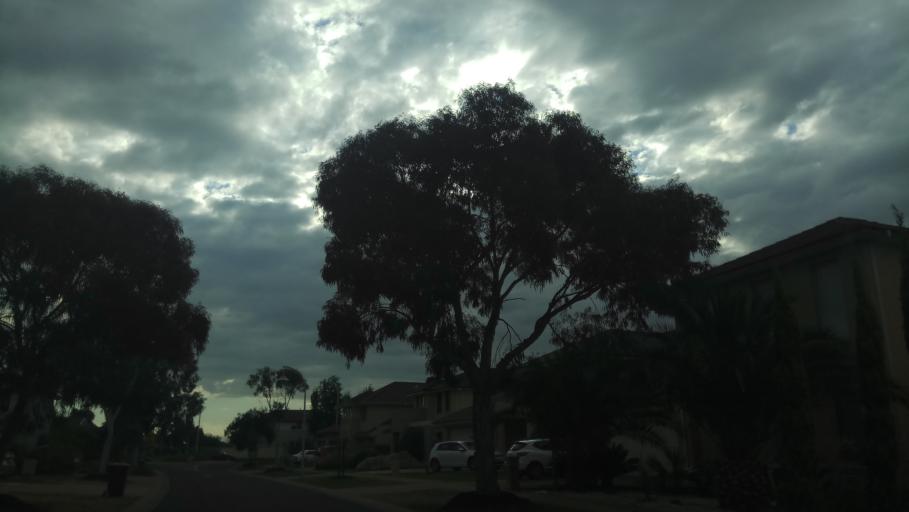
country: AU
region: Victoria
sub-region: Hobsons Bay
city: Altona Meadows
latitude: -37.8952
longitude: 144.7756
